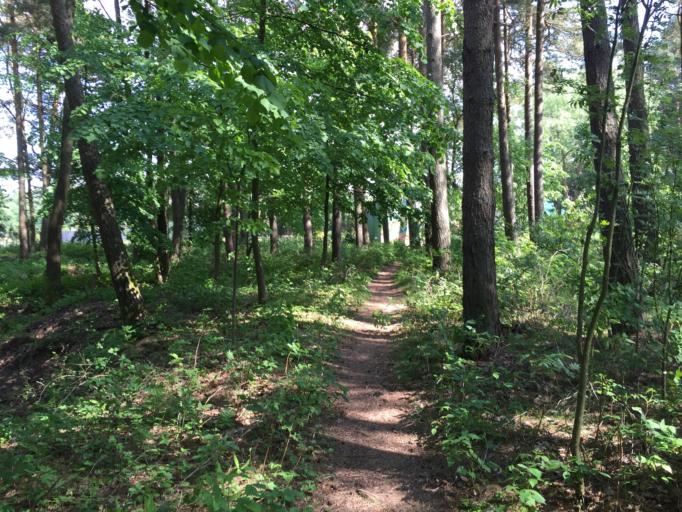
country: LT
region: Klaipedos apskritis
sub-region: Klaipeda
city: Palanga
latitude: 55.9293
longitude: 21.0626
